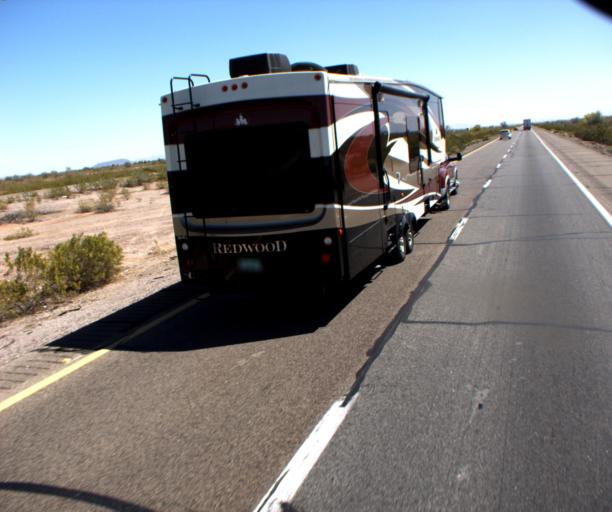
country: US
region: Arizona
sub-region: Maricopa County
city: Buckeye
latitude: 33.5072
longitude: -112.9922
